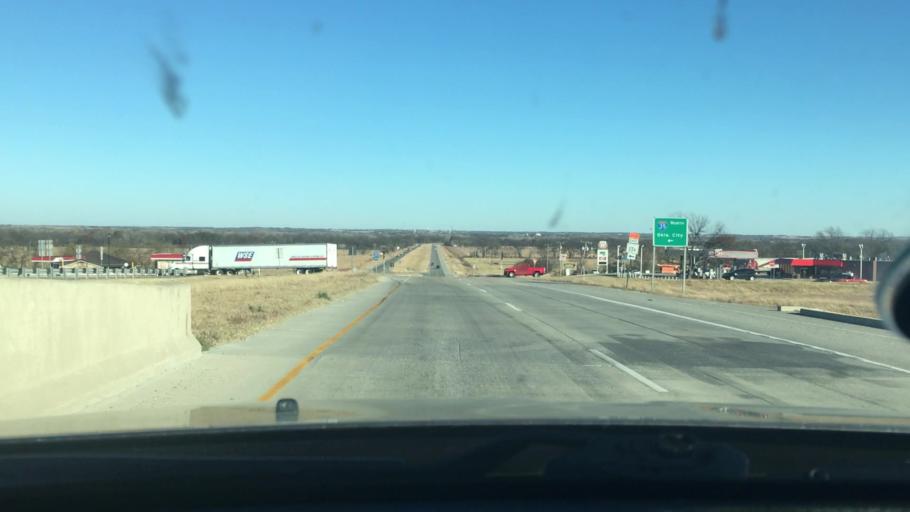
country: US
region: Oklahoma
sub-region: Murray County
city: Davis
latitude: 34.5064
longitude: -97.1737
